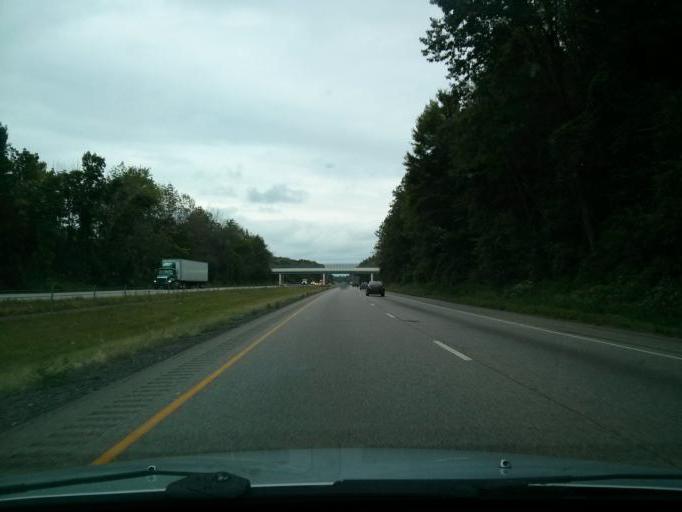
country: US
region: Ohio
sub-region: Portage County
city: Brimfield
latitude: 41.1088
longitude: -81.3165
